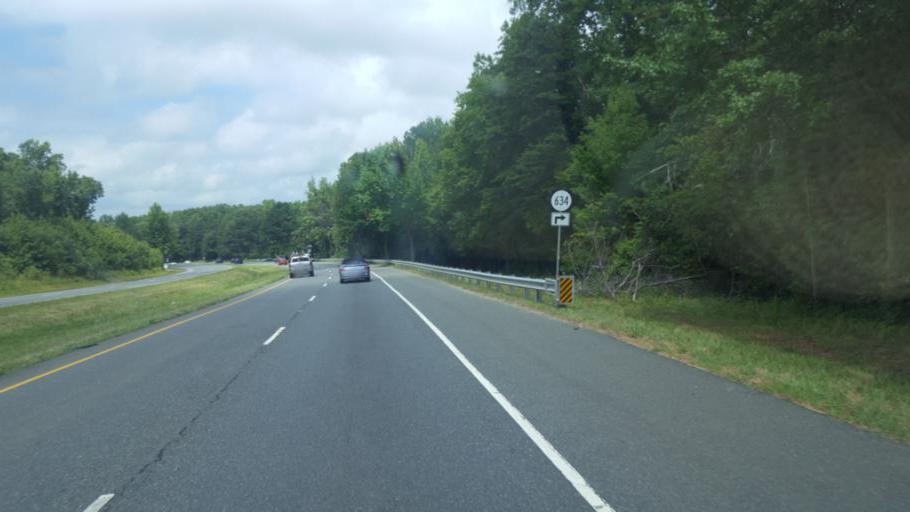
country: US
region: Virginia
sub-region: Stafford County
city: Falmouth
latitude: 38.3885
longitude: -77.5477
